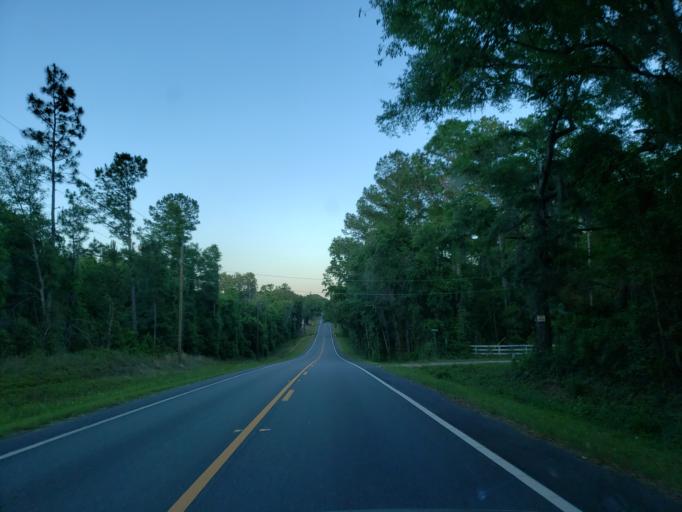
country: US
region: Georgia
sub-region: Echols County
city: Statenville
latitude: 30.5813
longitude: -83.2065
